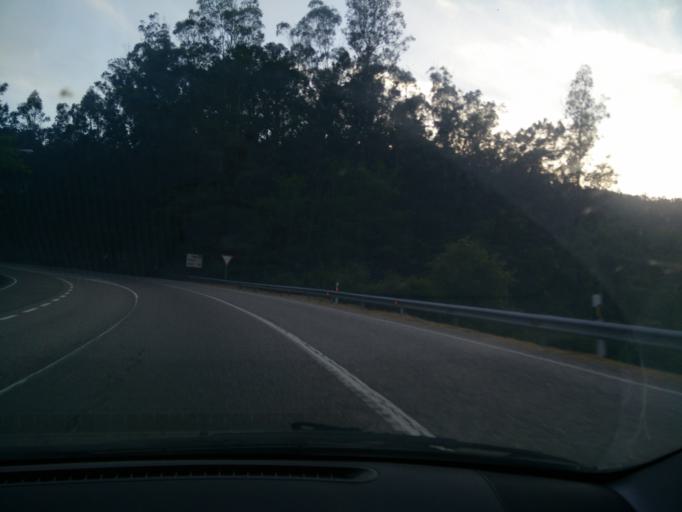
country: ES
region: Galicia
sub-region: Provincia de Pontevedra
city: Porrino
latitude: 42.1800
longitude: -8.5705
